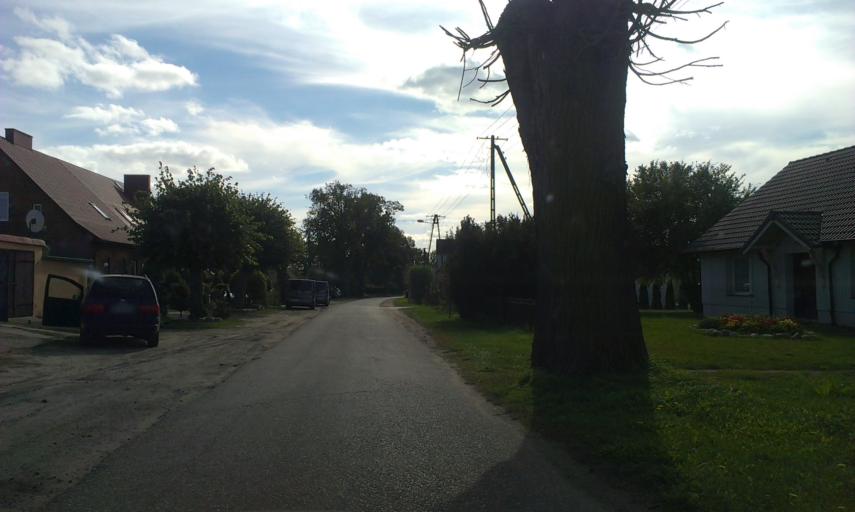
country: PL
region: Greater Poland Voivodeship
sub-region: Powiat zlotowski
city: Zlotow
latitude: 53.3055
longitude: 17.1293
